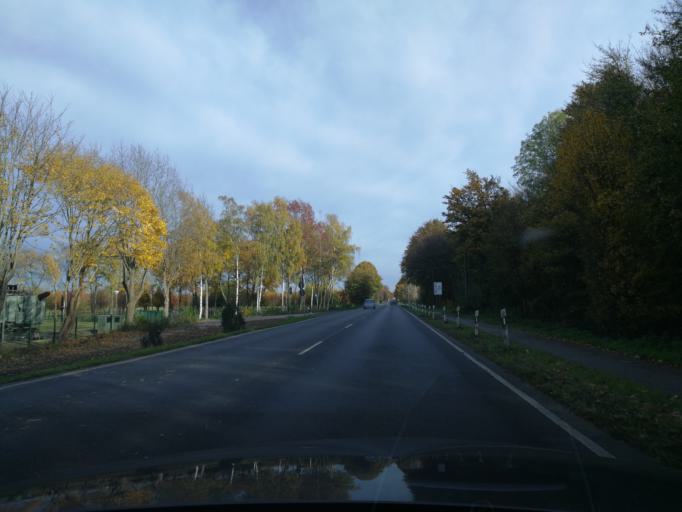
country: DE
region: North Rhine-Westphalia
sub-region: Regierungsbezirk Dusseldorf
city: Meerbusch
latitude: 51.2949
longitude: 6.6604
